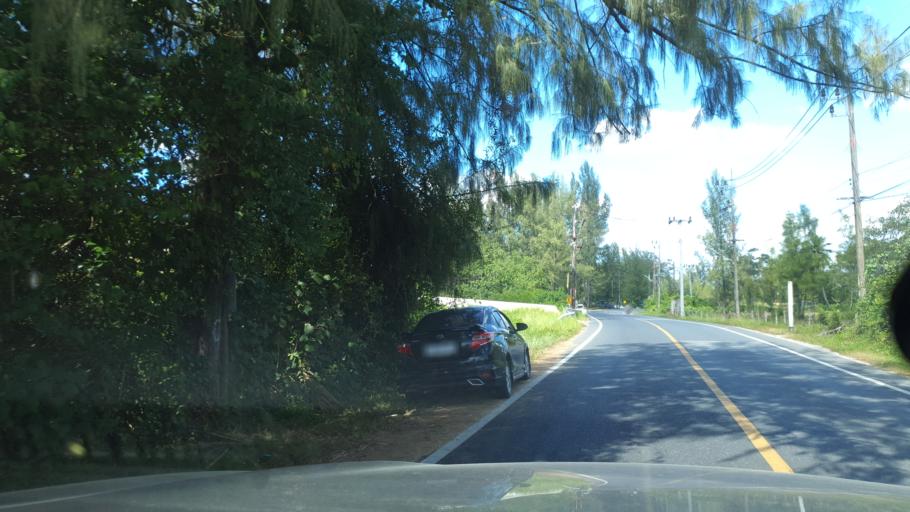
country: TH
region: Phangnga
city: Thai Mueang
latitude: 8.2827
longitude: 98.2755
